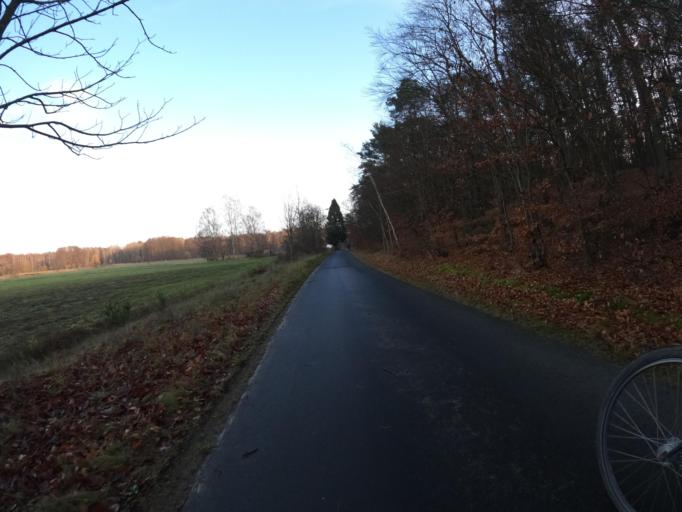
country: PL
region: West Pomeranian Voivodeship
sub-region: Powiat policki
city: Nowe Warpno
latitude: 53.6914
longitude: 14.2679
